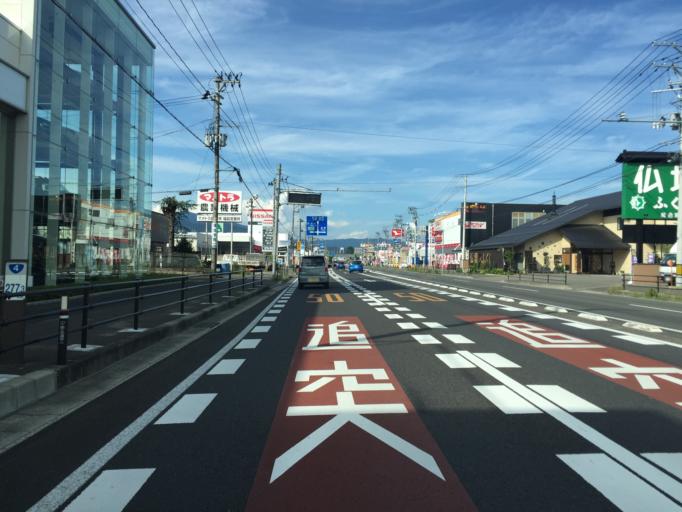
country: JP
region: Fukushima
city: Fukushima-shi
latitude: 37.7956
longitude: 140.4892
